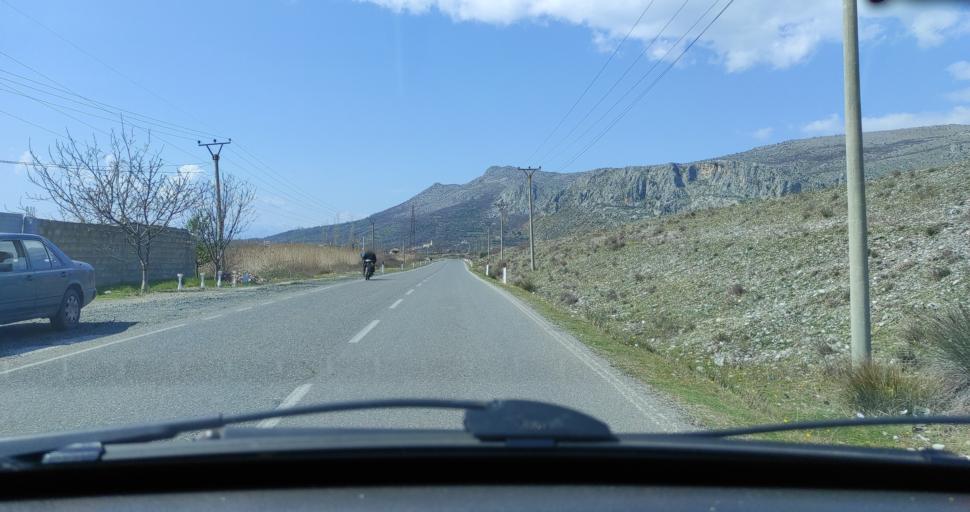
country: AL
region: Shkoder
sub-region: Rrethi i Shkodres
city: Vau i Dejes
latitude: 42.0046
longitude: 19.6238
